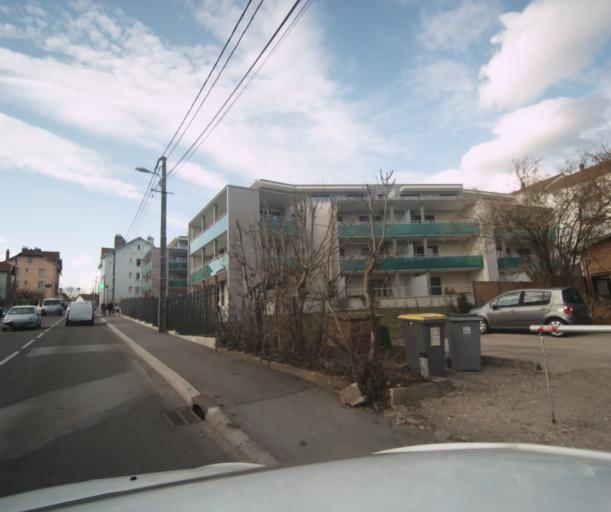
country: FR
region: Franche-Comte
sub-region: Departement du Doubs
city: Besancon
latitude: 47.2531
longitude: 6.0303
